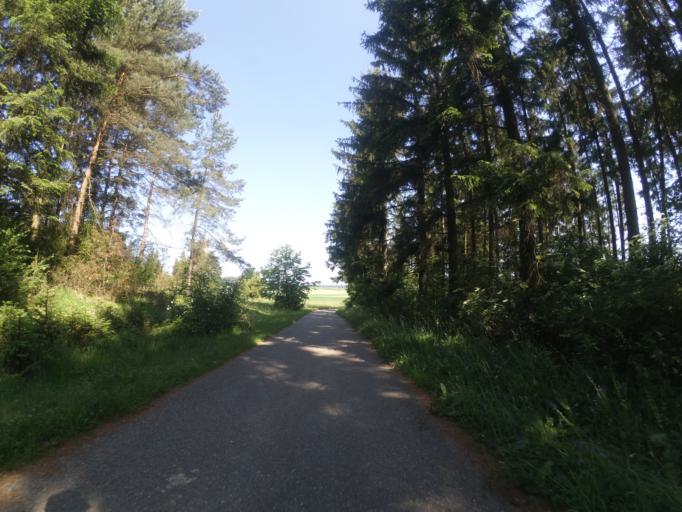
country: DE
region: Baden-Wuerttemberg
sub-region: Tuebingen Region
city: Bernstadt
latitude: 48.4858
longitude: 10.0142
